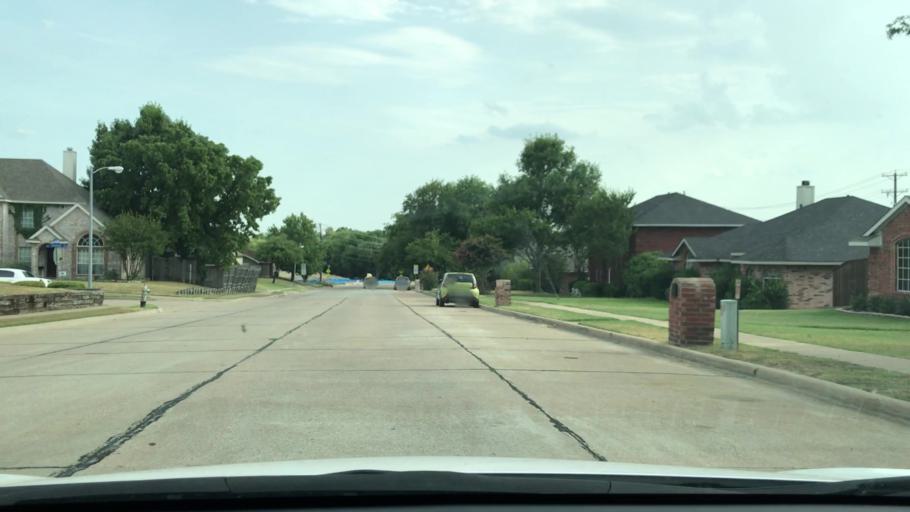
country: US
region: Texas
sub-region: Collin County
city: Wylie
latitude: 33.0130
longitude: -96.5201
